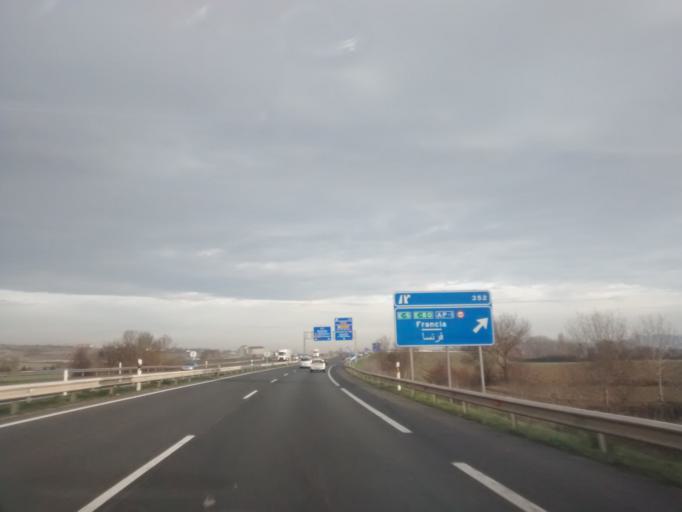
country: ES
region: Basque Country
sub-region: Provincia de Alava
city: Gasteiz / Vitoria
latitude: 42.8806
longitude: -2.7027
